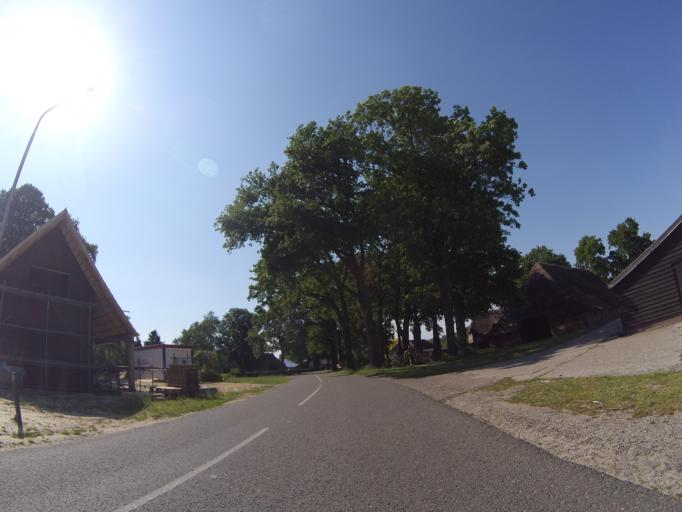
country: NL
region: Drenthe
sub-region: Gemeente Coevorden
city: Dalen
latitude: 52.7154
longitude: 6.8027
